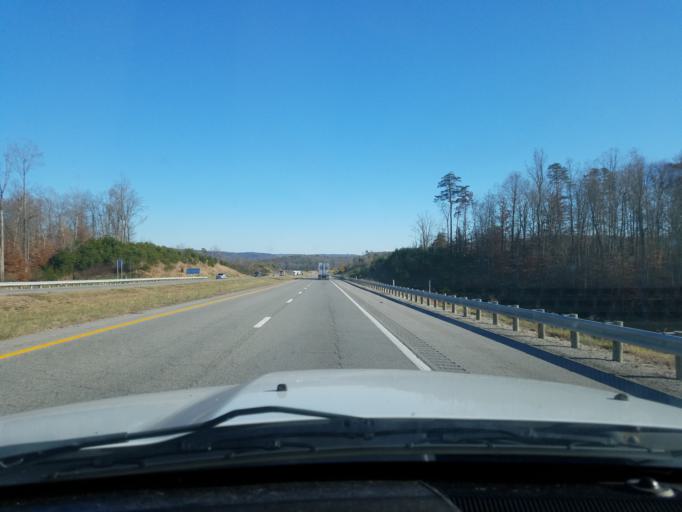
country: US
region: West Virginia
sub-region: Putnam County
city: Eleanor
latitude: 38.5517
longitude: -81.9894
